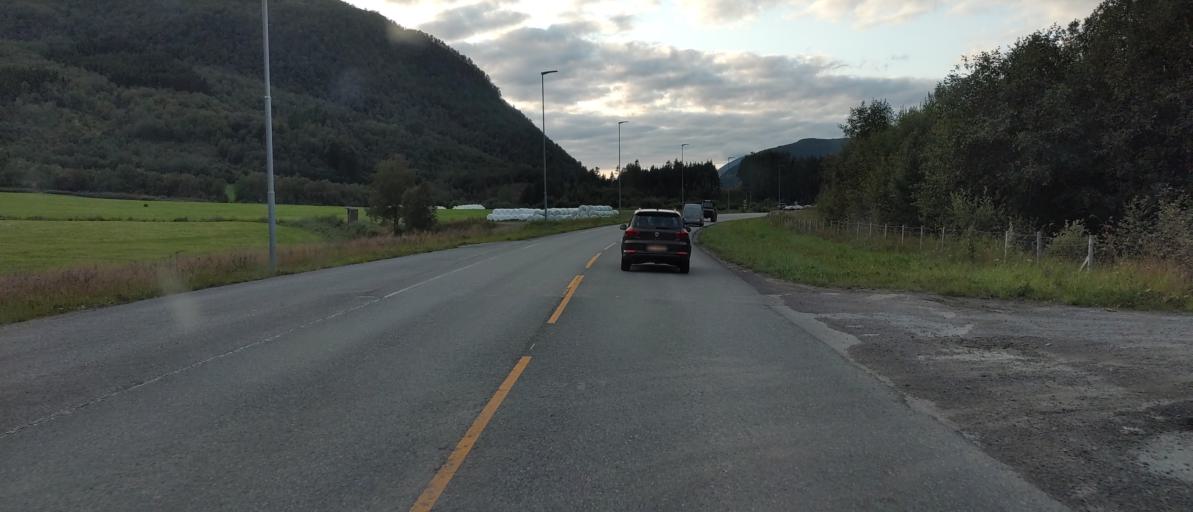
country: NO
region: More og Romsdal
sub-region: Molde
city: Molde
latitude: 62.7896
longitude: 7.2347
